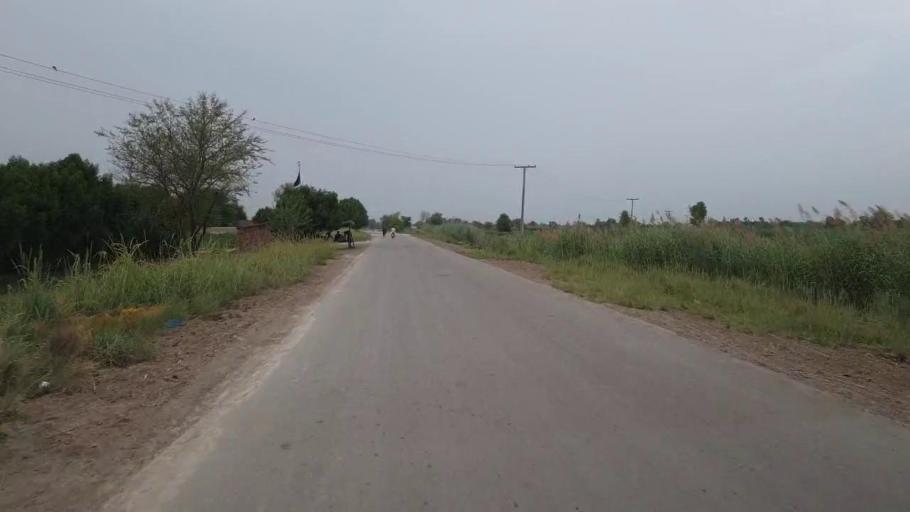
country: PK
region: Sindh
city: Bandhi
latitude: 26.5387
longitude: 68.2195
